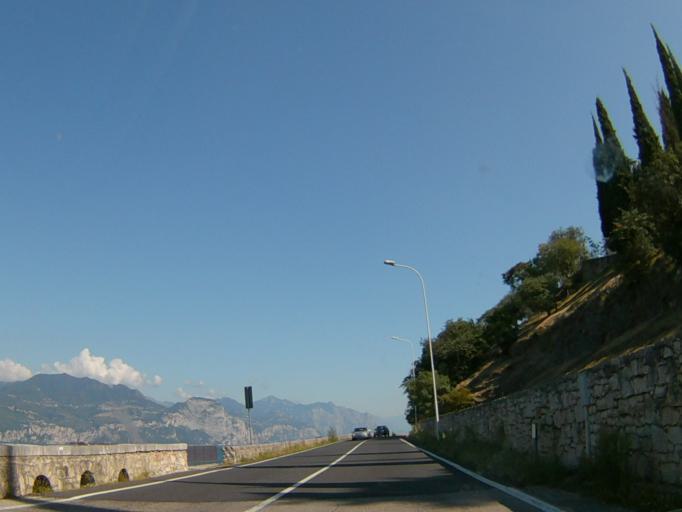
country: IT
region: Veneto
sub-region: Provincia di Verona
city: San Zeno di Montagna
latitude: 45.6604
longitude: 10.7263
